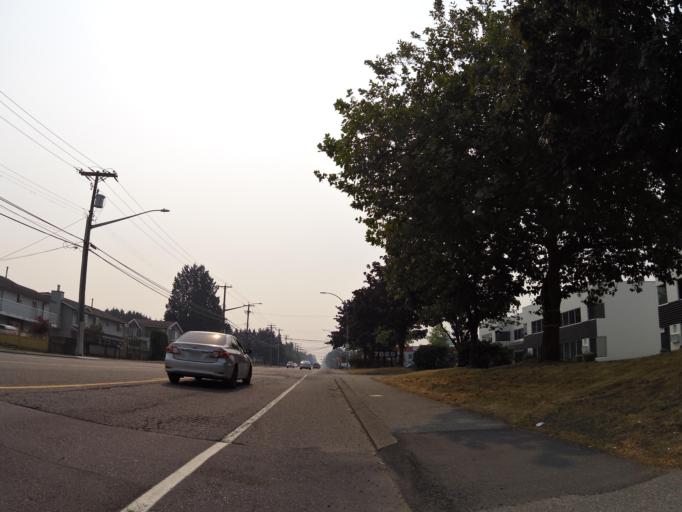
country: CA
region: British Columbia
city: Delta
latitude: 49.1466
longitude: -122.8568
